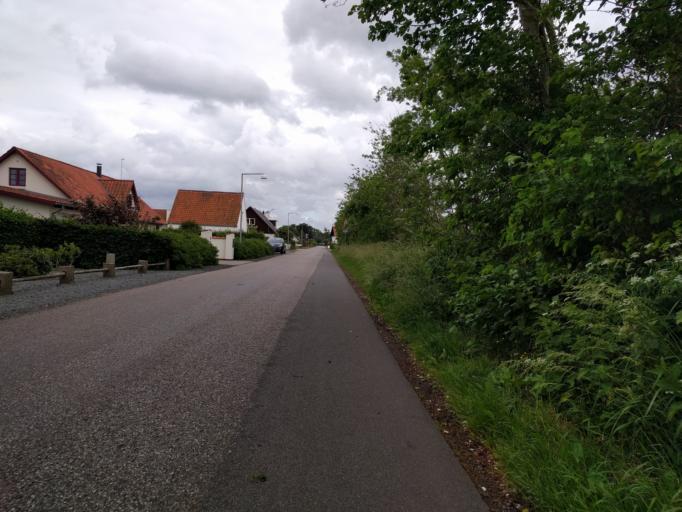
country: DK
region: South Denmark
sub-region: Kerteminde Kommune
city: Munkebo
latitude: 55.4263
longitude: 10.5245
